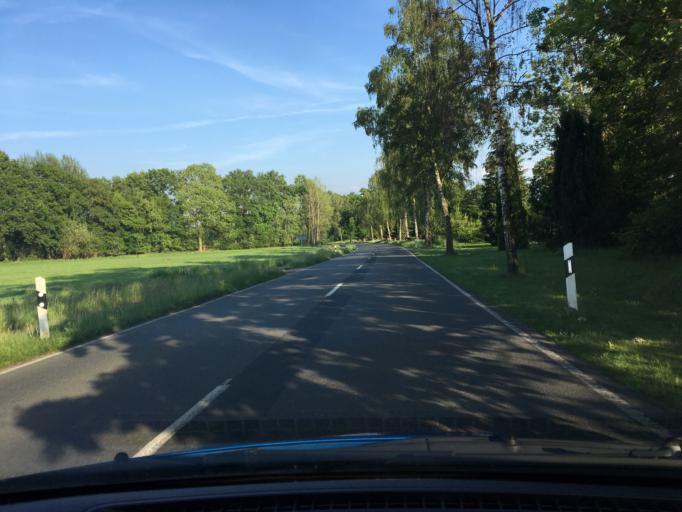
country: DE
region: Lower Saxony
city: Otter
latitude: 53.2590
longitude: 9.7410
